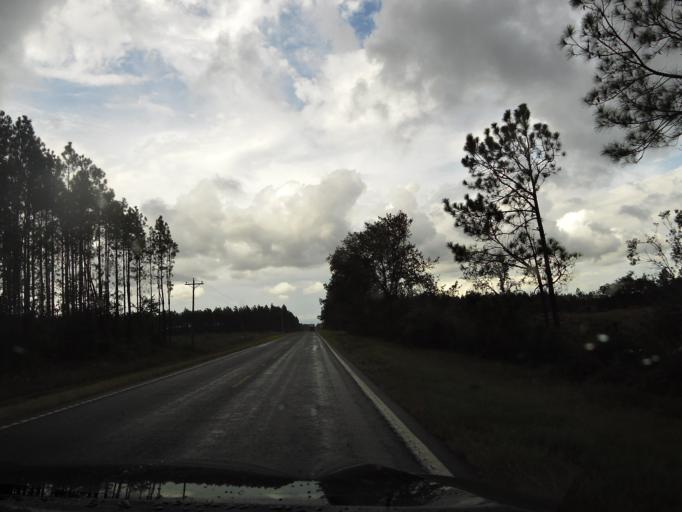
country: US
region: Florida
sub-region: Nassau County
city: Hilliard
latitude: 30.5567
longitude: -82.0422
